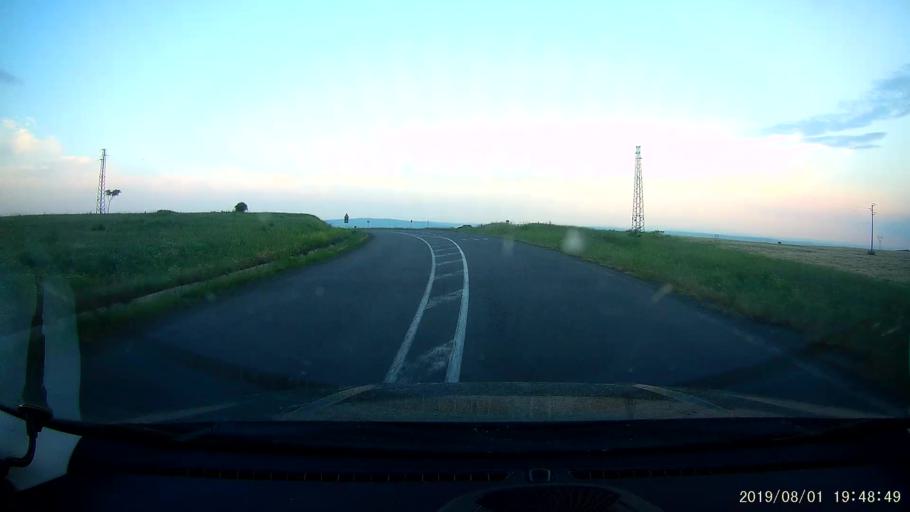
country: BG
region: Burgas
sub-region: Obshtina Karnobat
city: Karnobat
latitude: 42.6316
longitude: 26.9432
